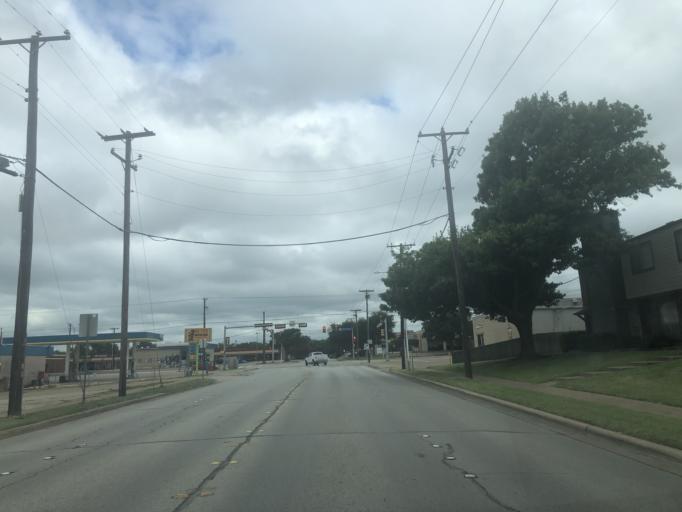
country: US
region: Texas
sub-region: Dallas County
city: Duncanville
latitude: 32.6517
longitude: -96.9245
